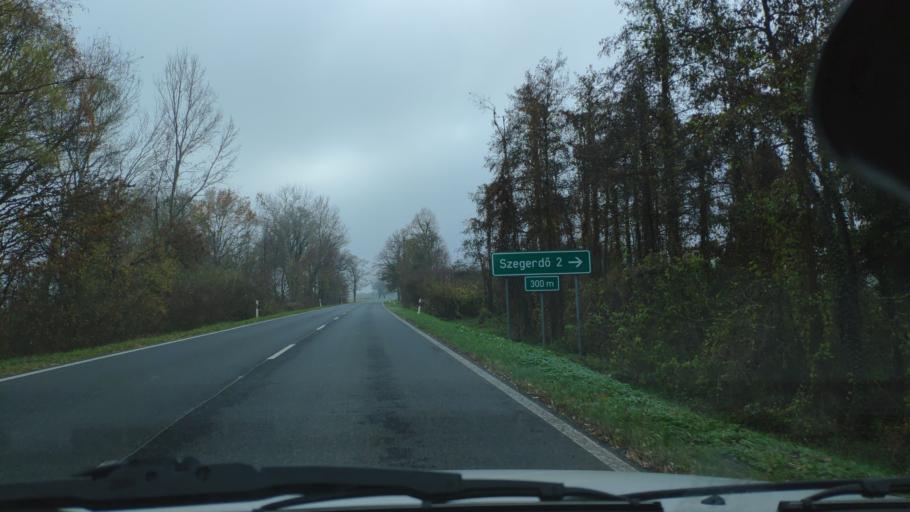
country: HU
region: Somogy
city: Balatonbereny
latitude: 46.6236
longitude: 17.2861
